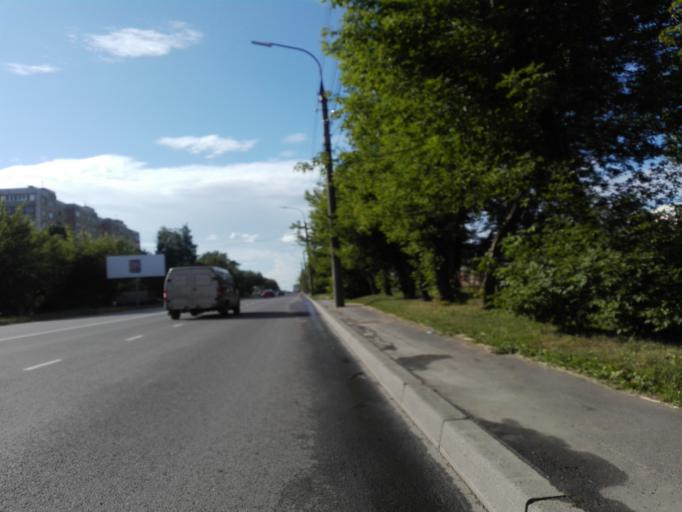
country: RU
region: Orjol
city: Orel
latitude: 52.9907
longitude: 36.1177
